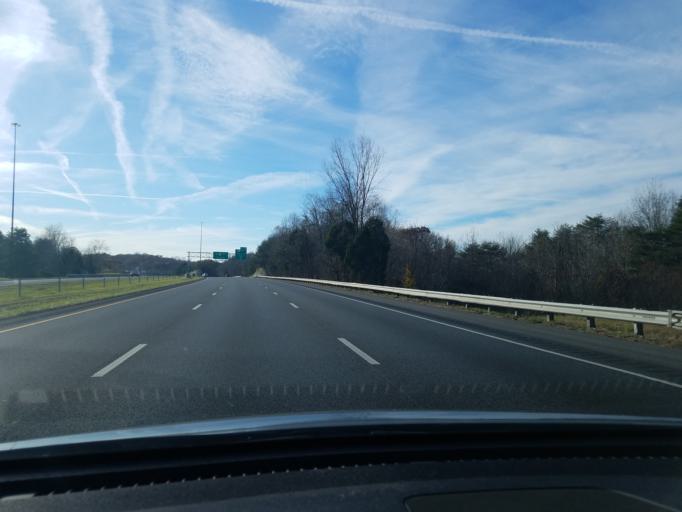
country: US
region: Indiana
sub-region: Floyd County
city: New Albany
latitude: 38.3042
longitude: -85.8837
